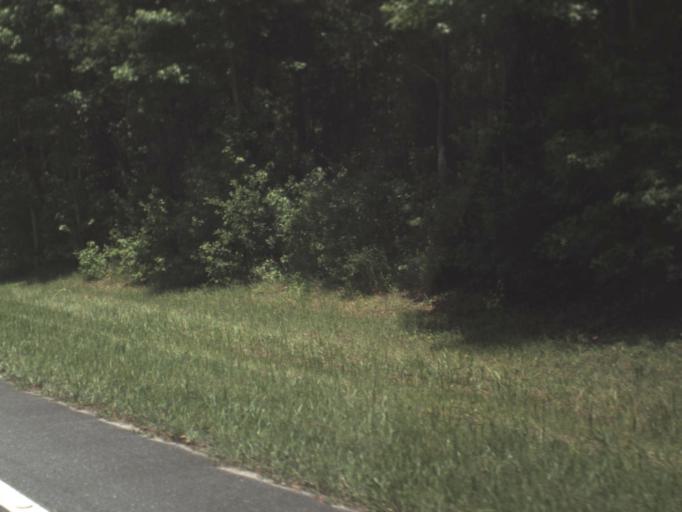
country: US
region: Florida
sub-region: Levy County
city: Williston
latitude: 29.4820
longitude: -82.4145
